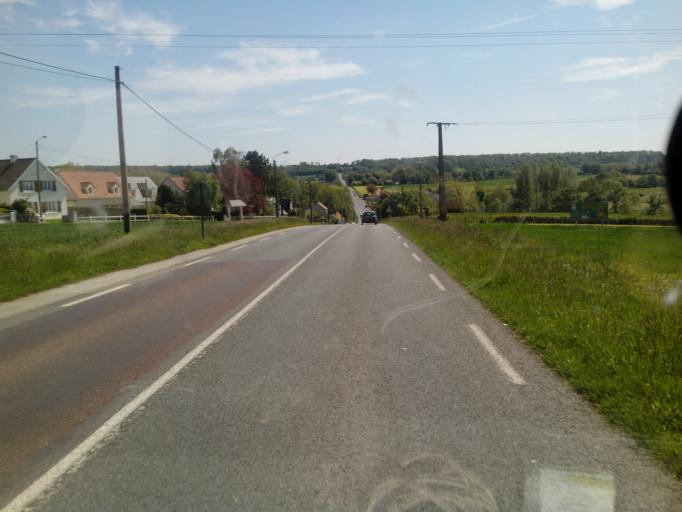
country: FR
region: Nord-Pas-de-Calais
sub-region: Departement du Pas-de-Calais
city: Samer
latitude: 50.6299
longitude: 1.7420
